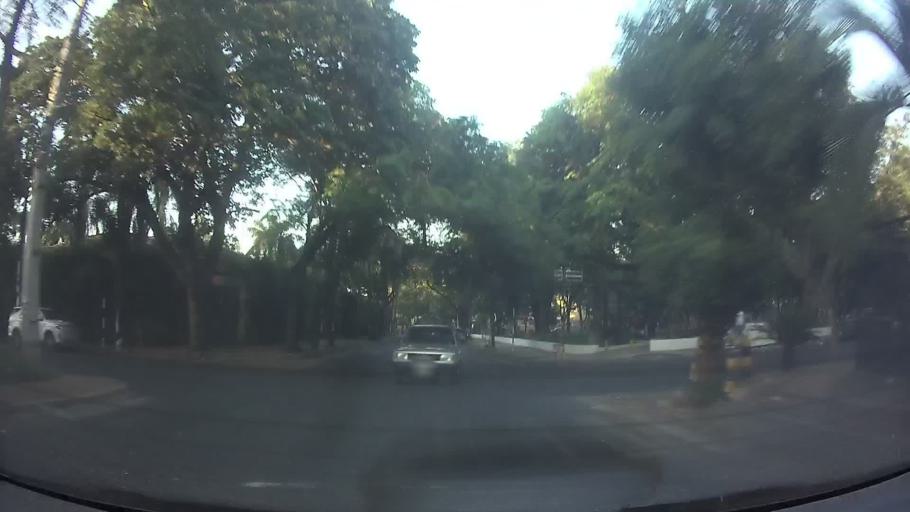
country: PY
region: Central
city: Lambare
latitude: -25.3092
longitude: -57.5784
